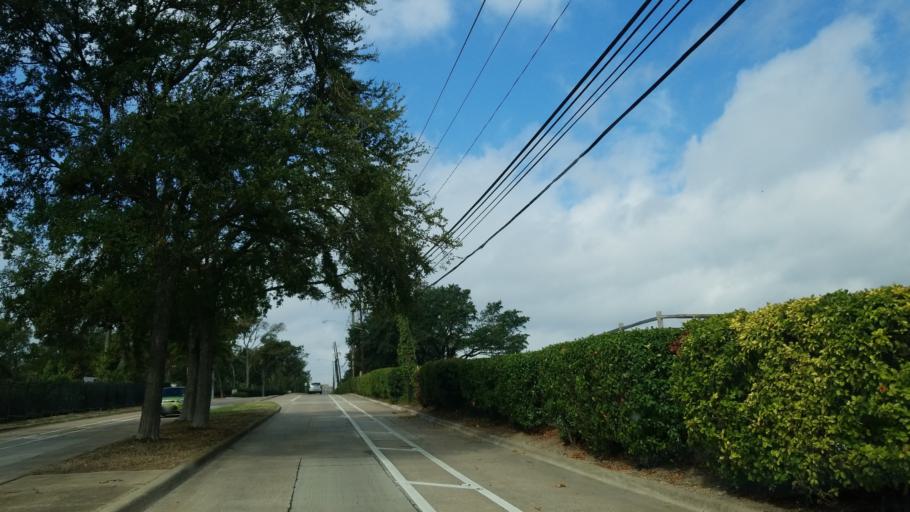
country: US
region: Texas
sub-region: Dallas County
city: Addison
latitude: 32.9332
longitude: -96.7920
